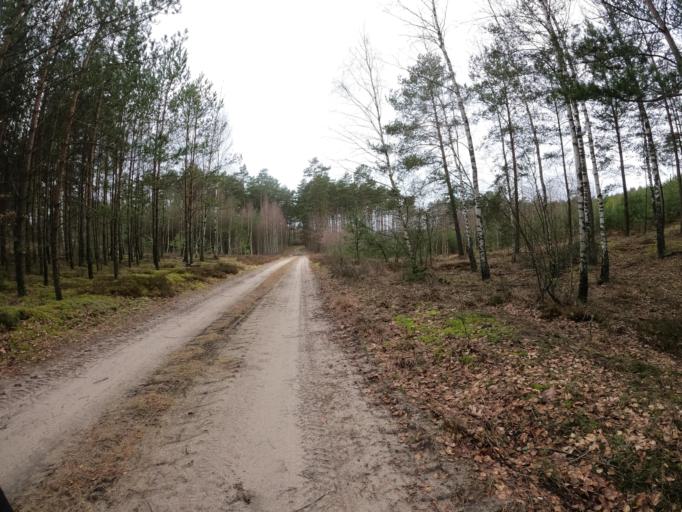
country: PL
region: Greater Poland Voivodeship
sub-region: Powiat zlotowski
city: Sypniewo
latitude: 53.4846
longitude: 16.5306
